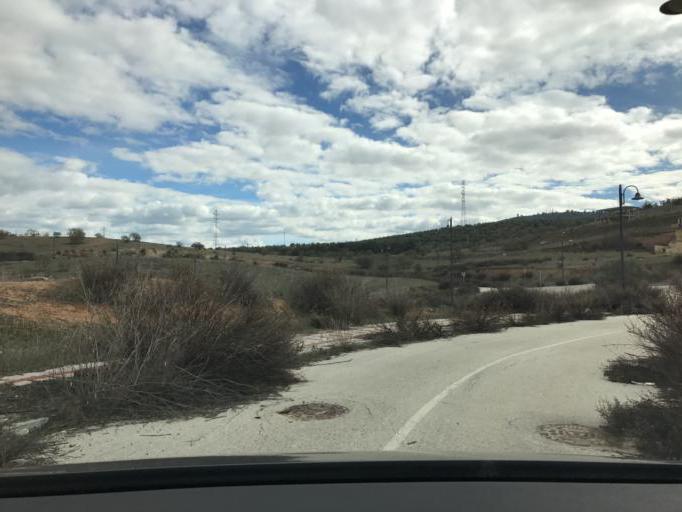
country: ES
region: Andalusia
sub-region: Provincia de Granada
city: Atarfe
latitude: 37.2583
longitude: -3.6957
